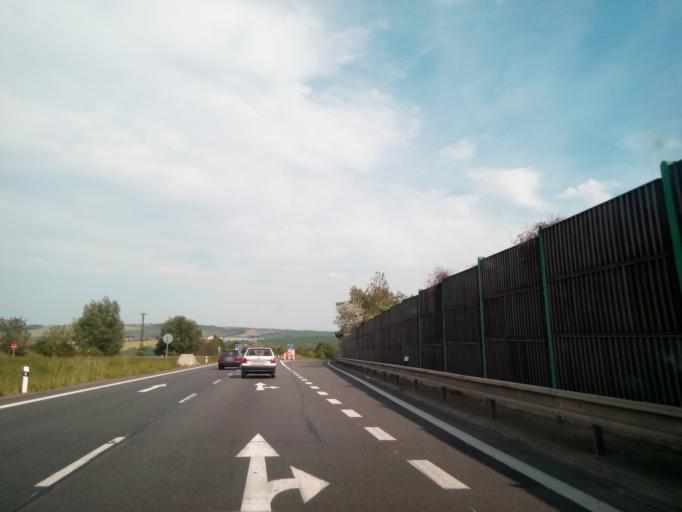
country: CZ
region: South Moravian
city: Blazovice
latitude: 49.1797
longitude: 16.8143
